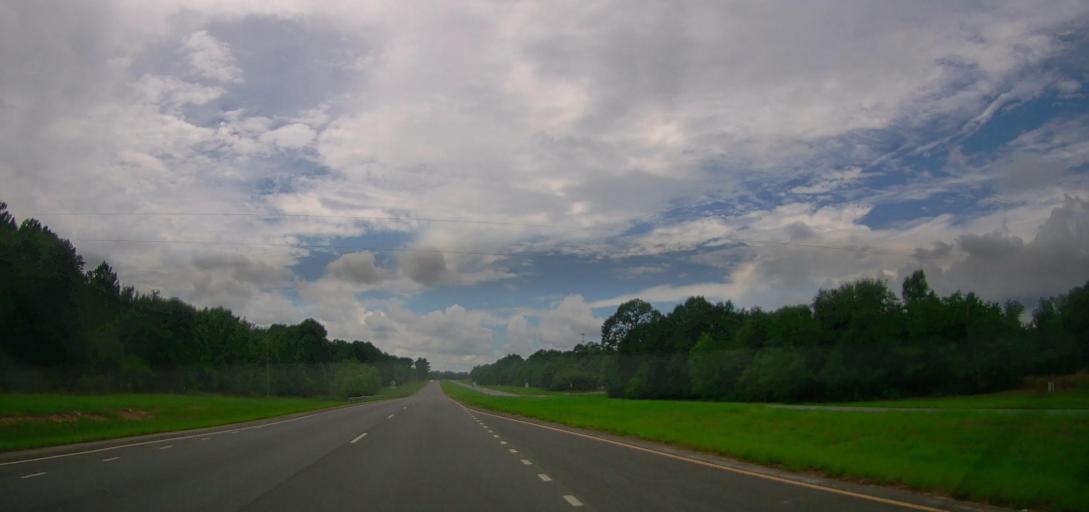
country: US
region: Georgia
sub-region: Telfair County
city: Helena
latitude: 32.1023
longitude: -83.0402
